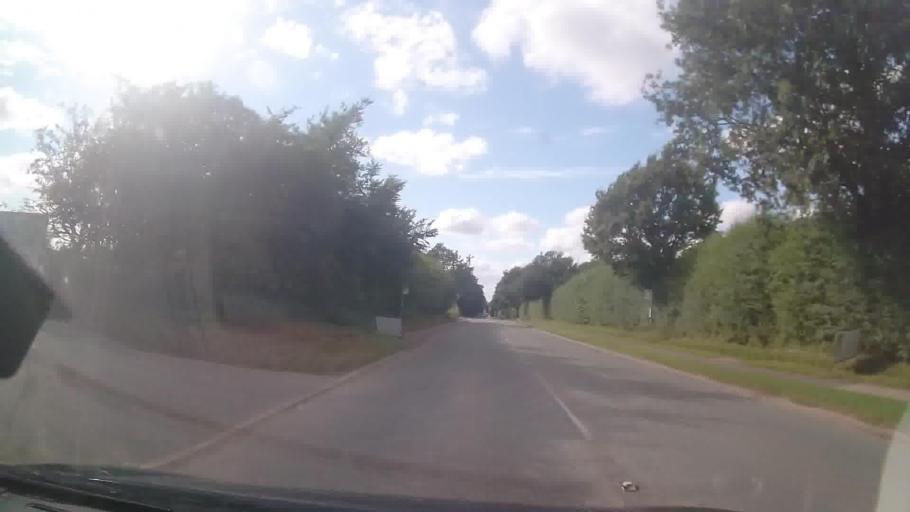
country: GB
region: England
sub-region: Shropshire
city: Bicton
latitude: 52.7200
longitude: -2.7970
